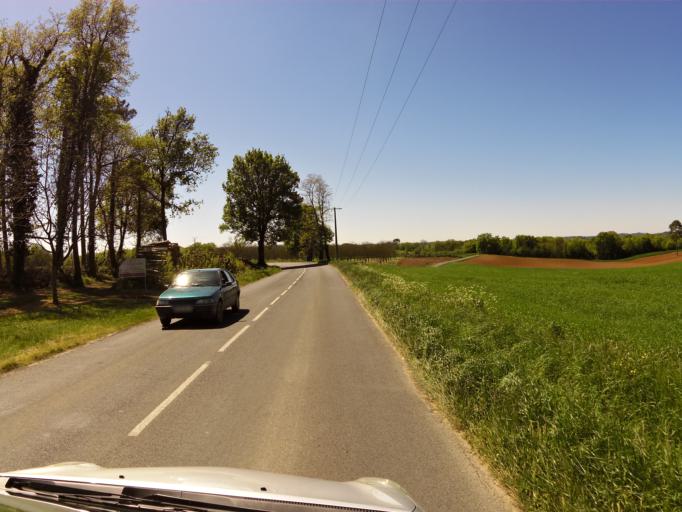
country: FR
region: Aquitaine
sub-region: Departement de la Dordogne
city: Eyvigues-et-Eybenes
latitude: 44.9731
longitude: 1.2875
